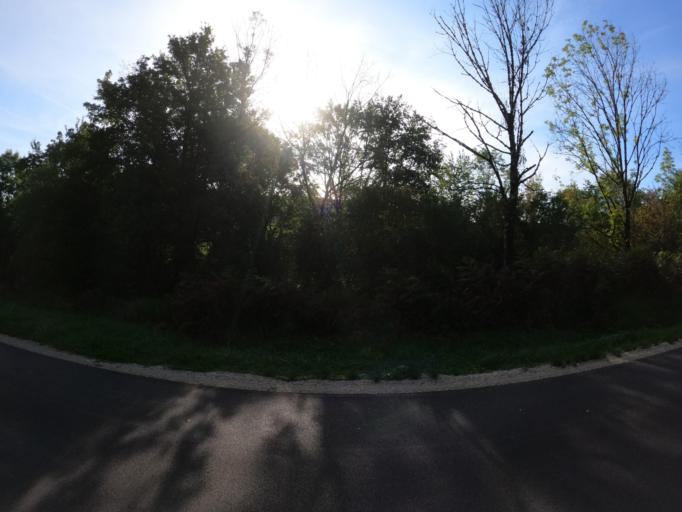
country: FR
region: Franche-Comte
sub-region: Departement du Jura
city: Montmorot
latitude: 46.7182
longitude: 5.5210
